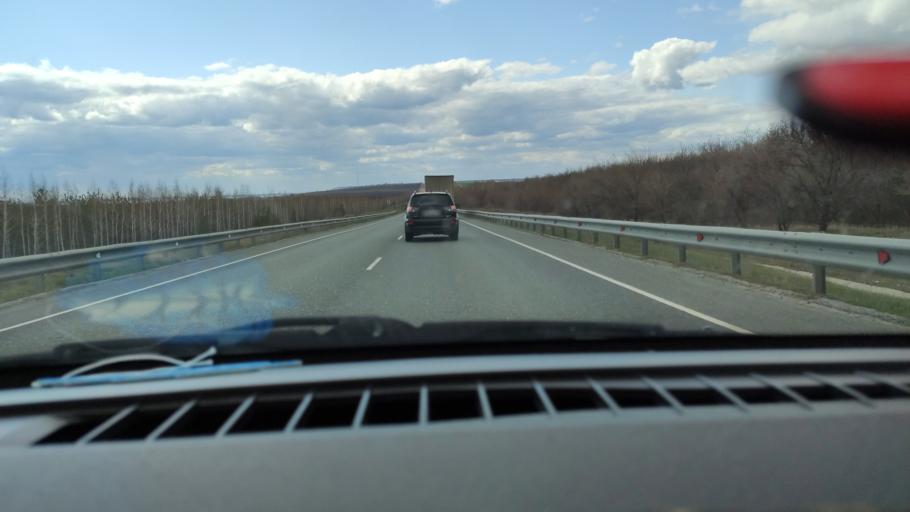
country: RU
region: Saratov
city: Balakovo
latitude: 52.1495
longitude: 47.8099
